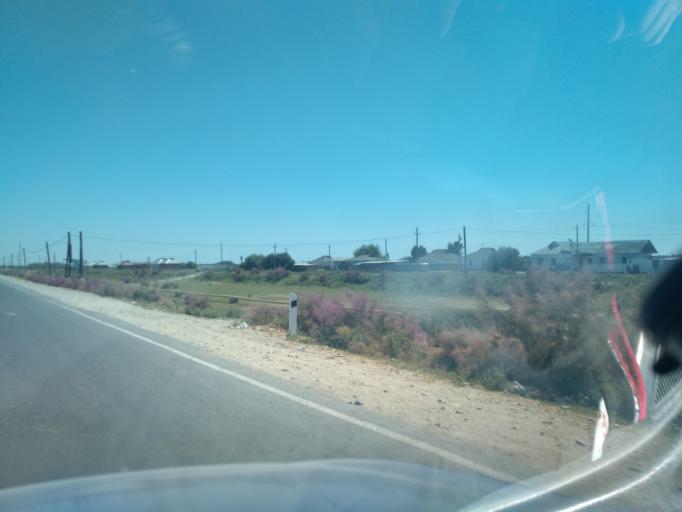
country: UZ
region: Sirdaryo
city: Guliston
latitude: 40.4910
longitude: 68.7084
